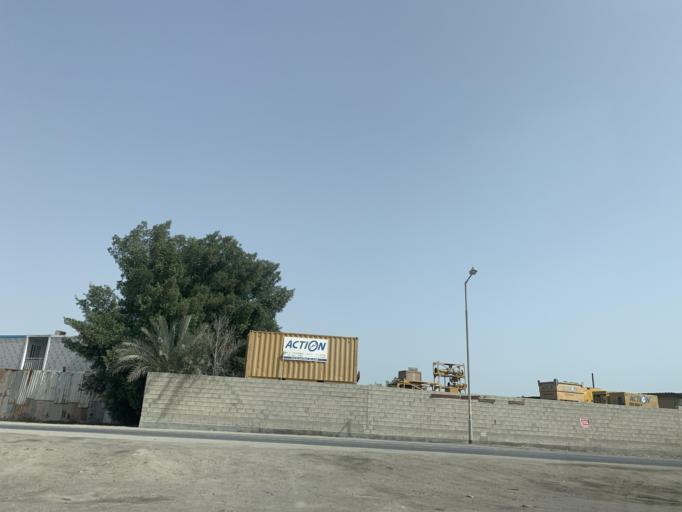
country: BH
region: Northern
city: Sitrah
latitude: 26.1350
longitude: 50.5951
